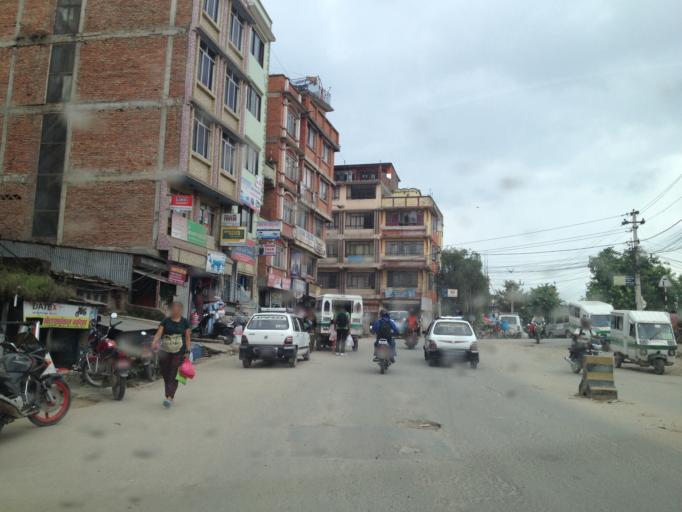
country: NP
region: Central Region
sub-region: Bagmati Zone
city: Kathmandu
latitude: 27.7012
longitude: 85.3020
